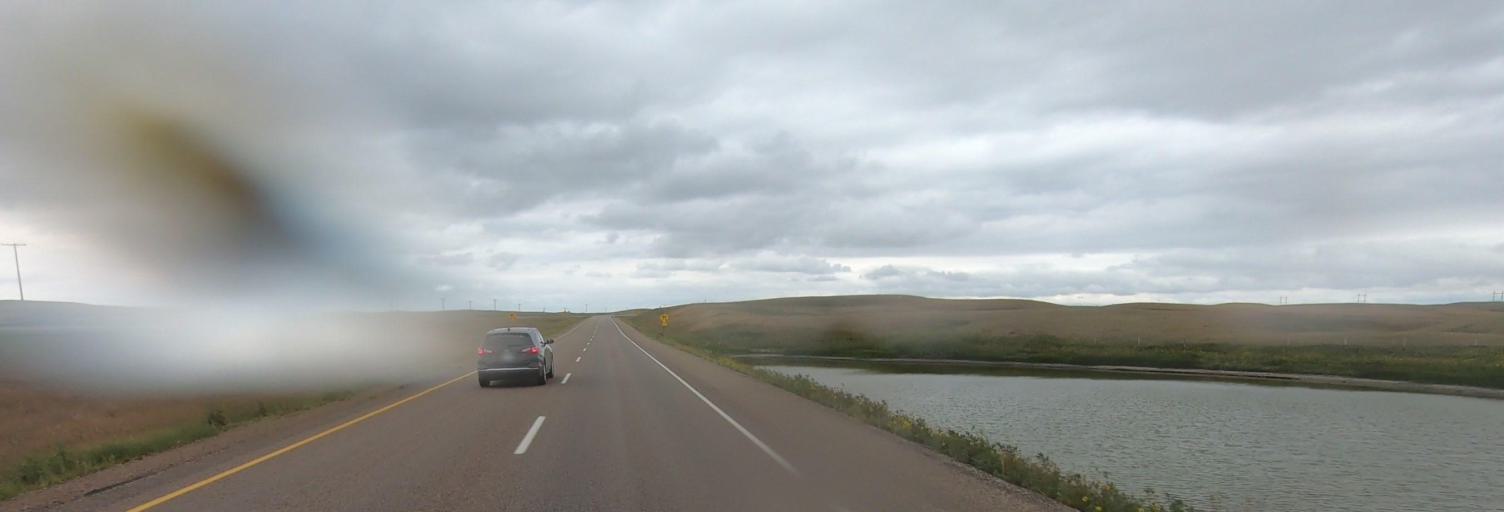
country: CA
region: Saskatchewan
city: Gravelbourg
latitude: 50.4630
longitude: -106.4866
